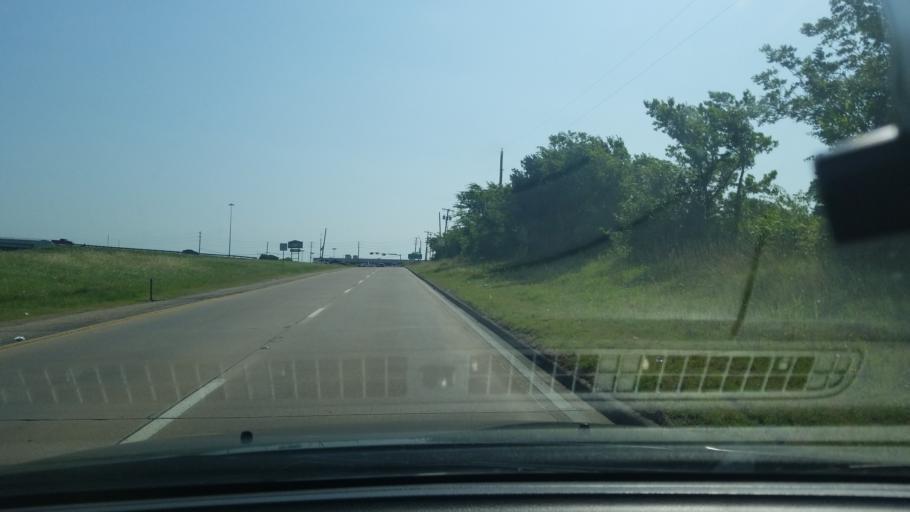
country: US
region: Texas
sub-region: Dallas County
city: Mesquite
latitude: 32.8237
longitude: -96.6258
